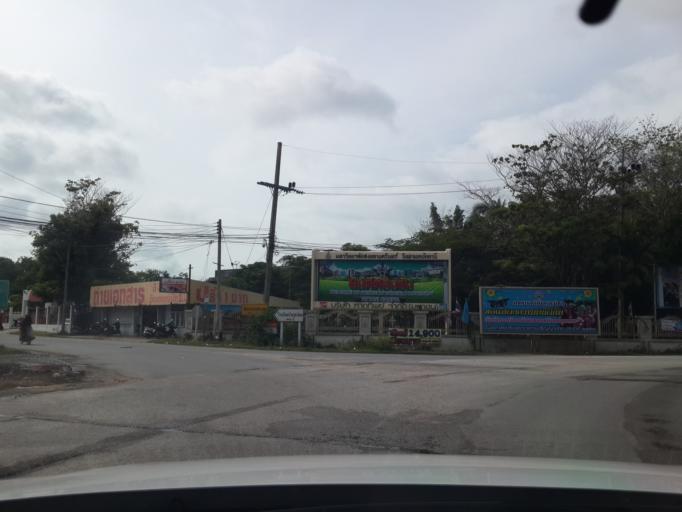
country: TH
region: Pattani
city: Pattani
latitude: 6.8770
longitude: 101.2345
